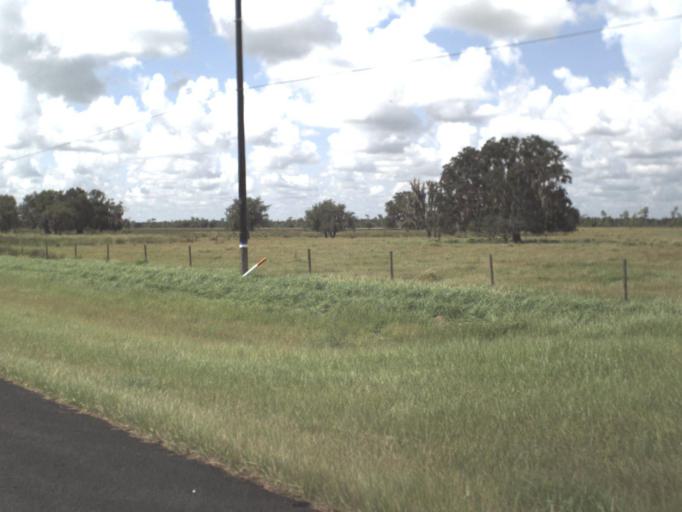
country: US
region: Florida
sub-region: Hardee County
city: Zolfo Springs
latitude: 27.4449
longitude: -81.7968
